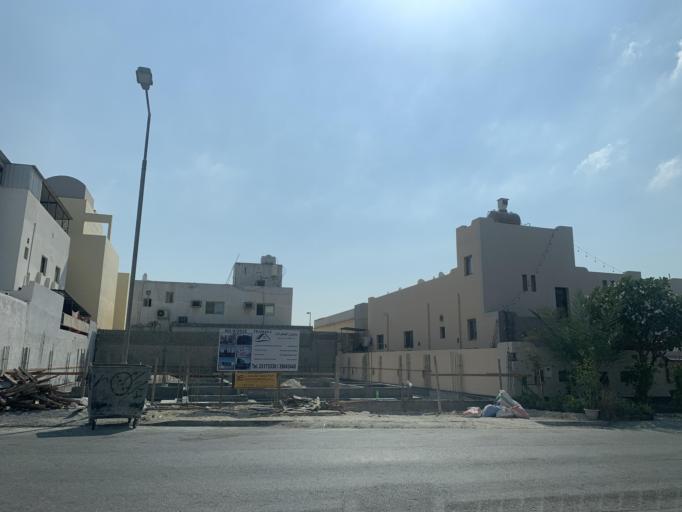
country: BH
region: Central Governorate
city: Madinat Hamad
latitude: 26.1096
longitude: 50.4979
